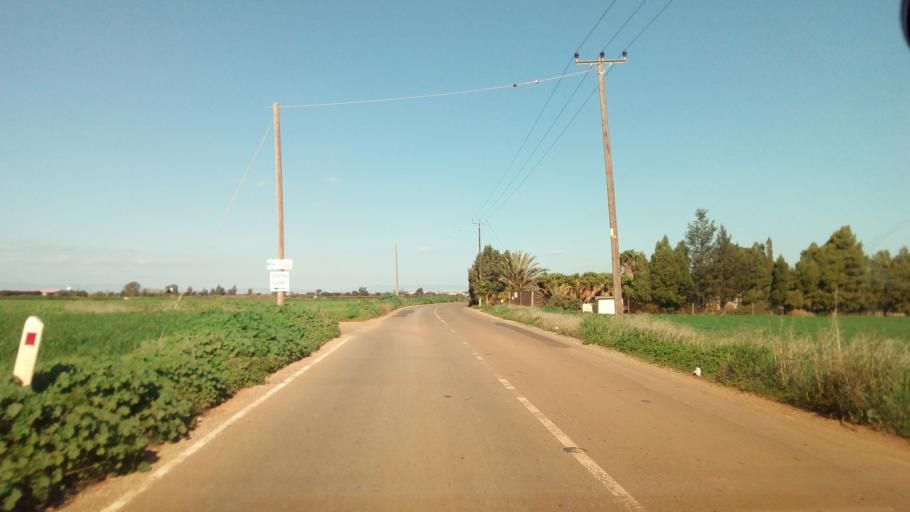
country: CY
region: Ammochostos
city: Avgorou
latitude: 35.0014
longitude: 33.8441
